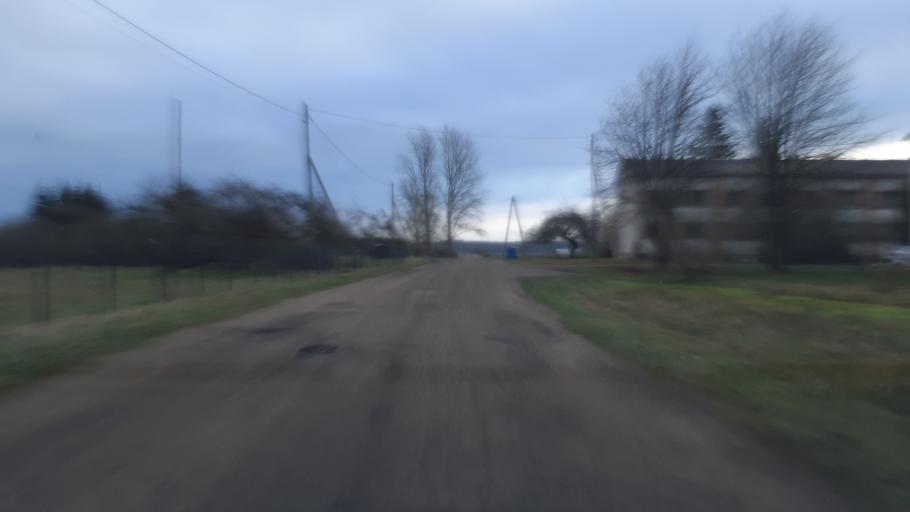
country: LV
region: Aizpute
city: Aizpute
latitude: 56.7997
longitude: 21.6676
